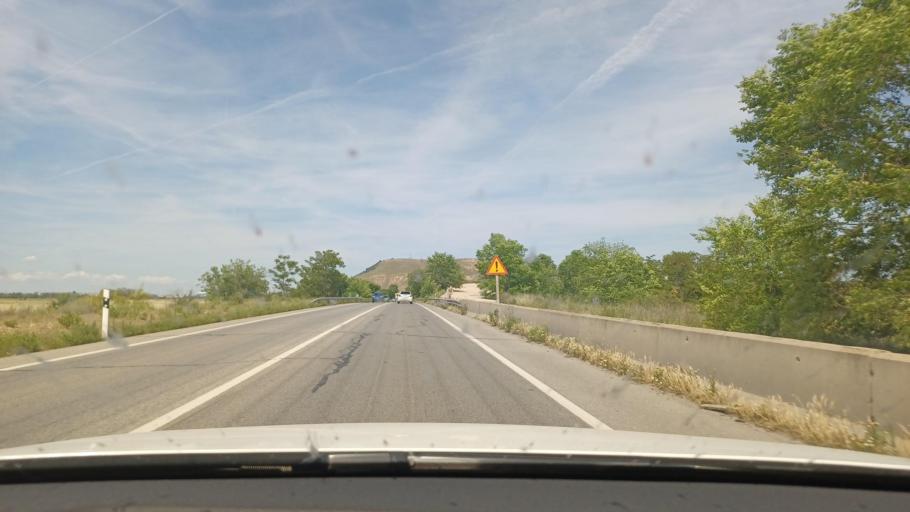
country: ES
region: Madrid
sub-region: Provincia de Madrid
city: Torrejon de Ardoz
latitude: 40.4344
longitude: -3.4372
